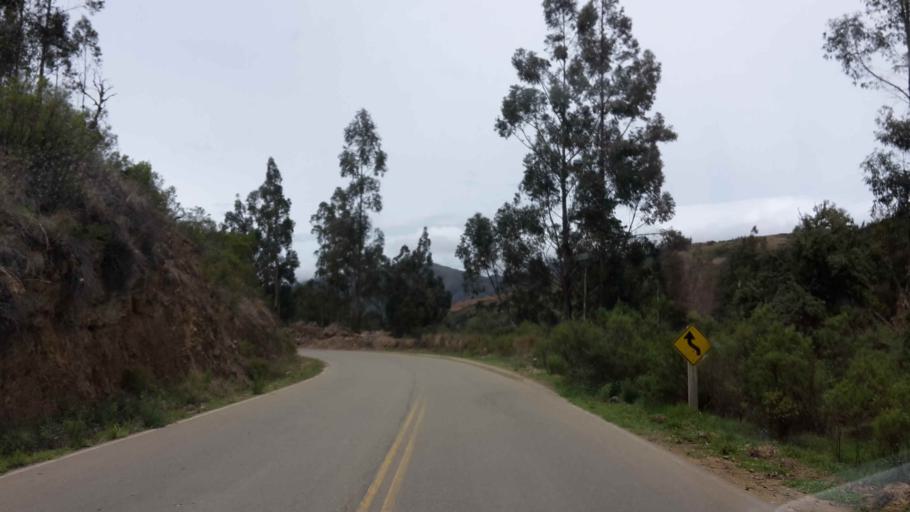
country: BO
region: Cochabamba
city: Totora
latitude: -17.6783
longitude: -65.2173
